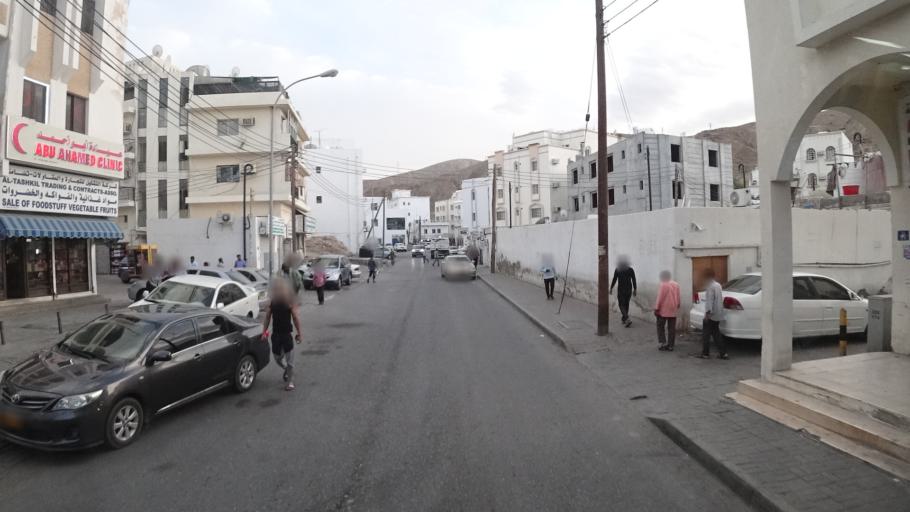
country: OM
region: Muhafazat Masqat
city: Muscat
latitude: 23.5818
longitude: 58.5456
